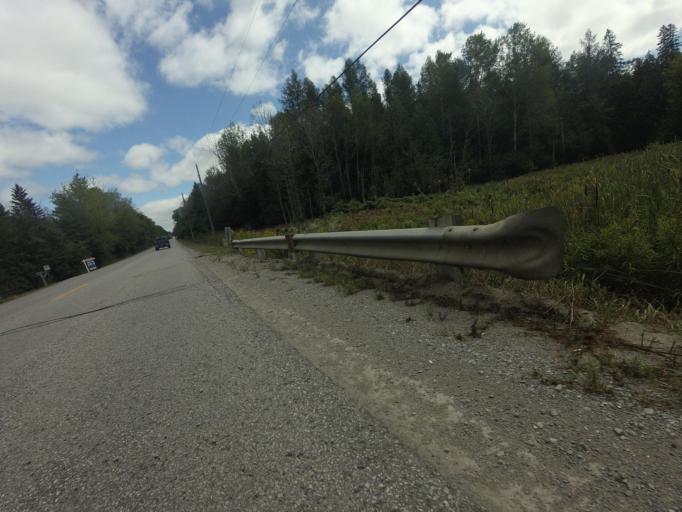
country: CA
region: Ontario
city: Uxbridge
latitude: 44.1075
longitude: -79.2481
